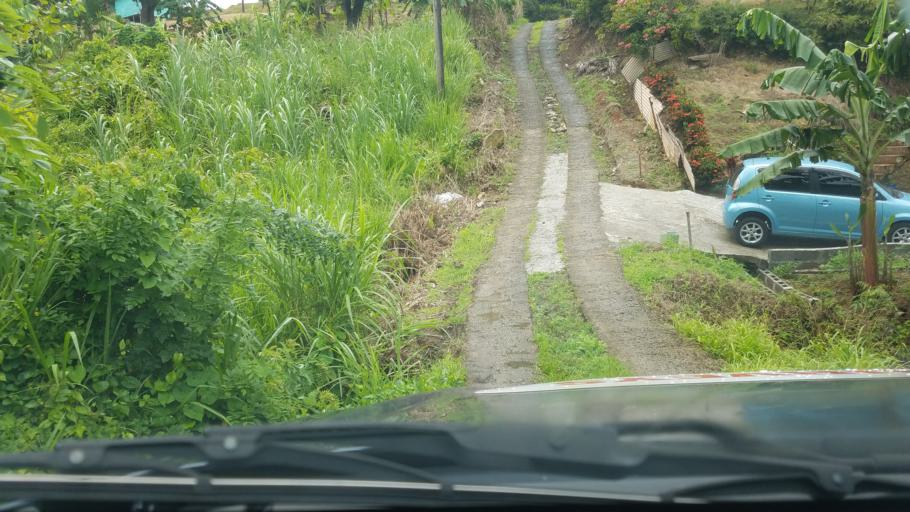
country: LC
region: Castries Quarter
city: Bisee
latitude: 13.9986
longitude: -60.9660
